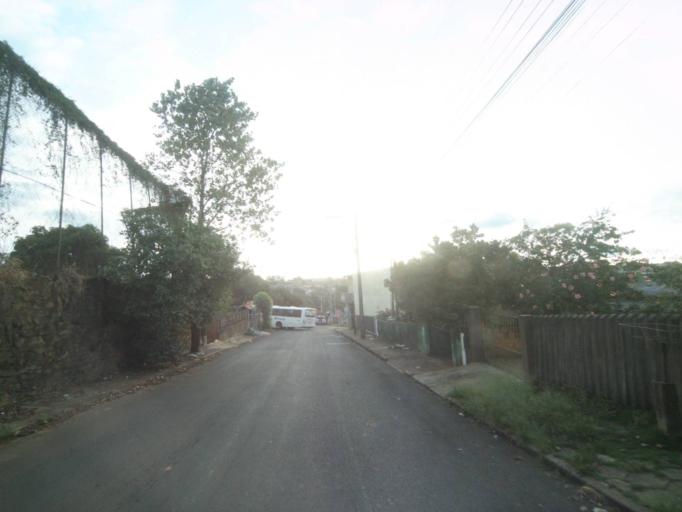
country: BR
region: Parana
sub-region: Telemaco Borba
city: Telemaco Borba
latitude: -24.3244
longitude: -50.6423
